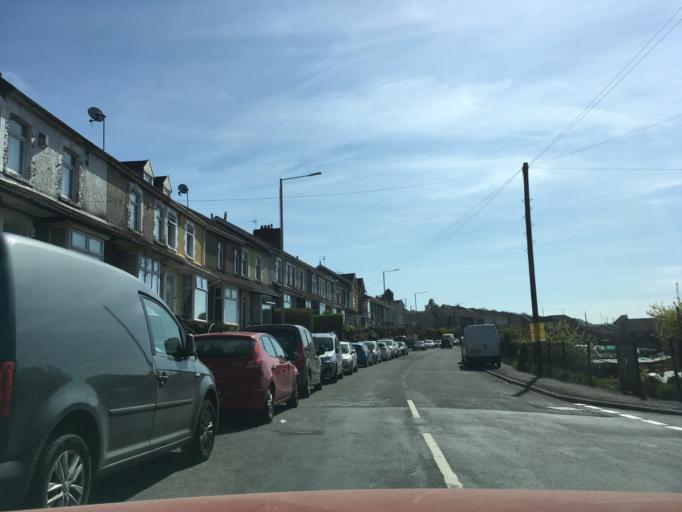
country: GB
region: Wales
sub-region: Rhondda Cynon Taf
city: Pontypridd
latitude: 51.6099
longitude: -3.3266
